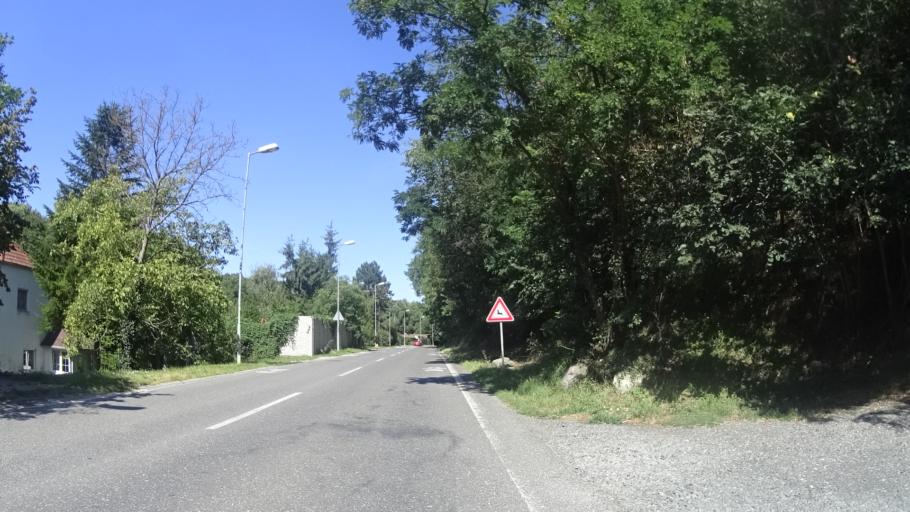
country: AT
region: Lower Austria
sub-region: Politischer Bezirk Bruck an der Leitha
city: Wolfsthal
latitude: 48.1533
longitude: 17.0225
